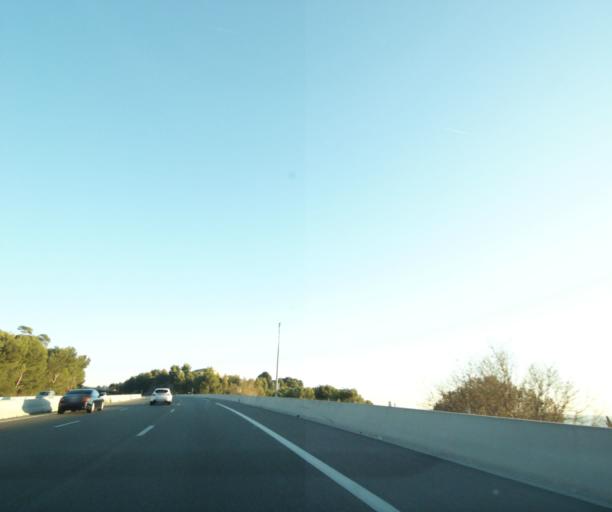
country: FR
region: Provence-Alpes-Cote d'Azur
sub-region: Departement des Bouches-du-Rhone
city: Ceyreste
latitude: 43.2015
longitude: 5.6334
